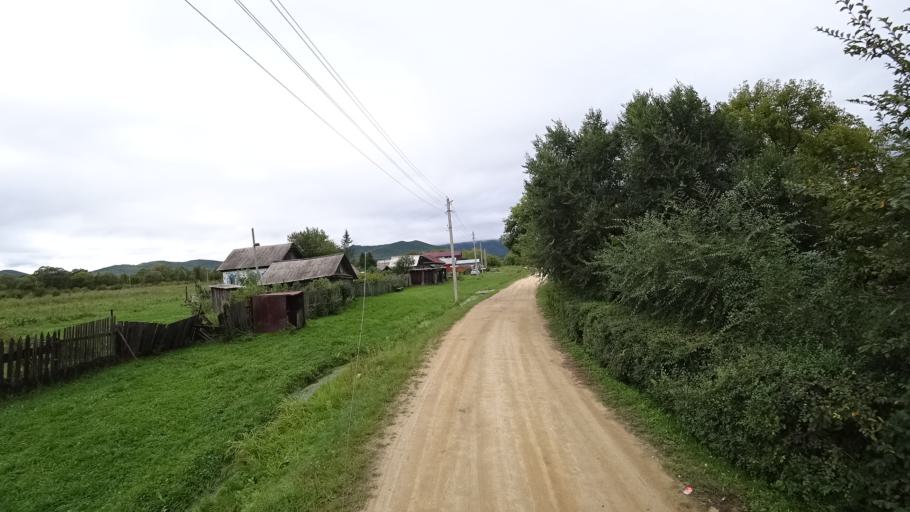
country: RU
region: Primorskiy
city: Rettikhovka
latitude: 44.1334
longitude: 132.6441
